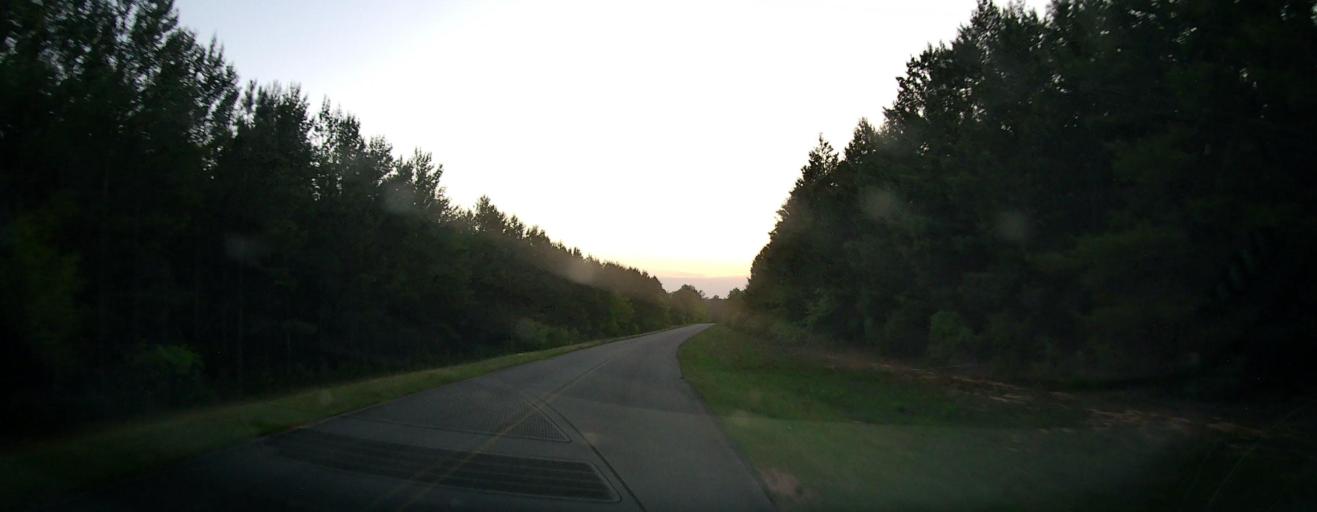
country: US
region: Georgia
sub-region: Marion County
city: Buena Vista
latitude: 32.2595
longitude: -84.5653
